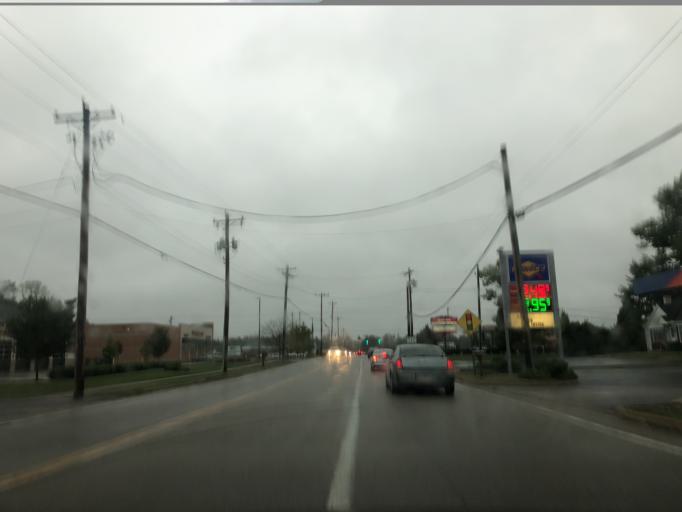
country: US
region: Ohio
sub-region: Clermont County
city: Mulberry
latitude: 39.2279
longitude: -84.2550
